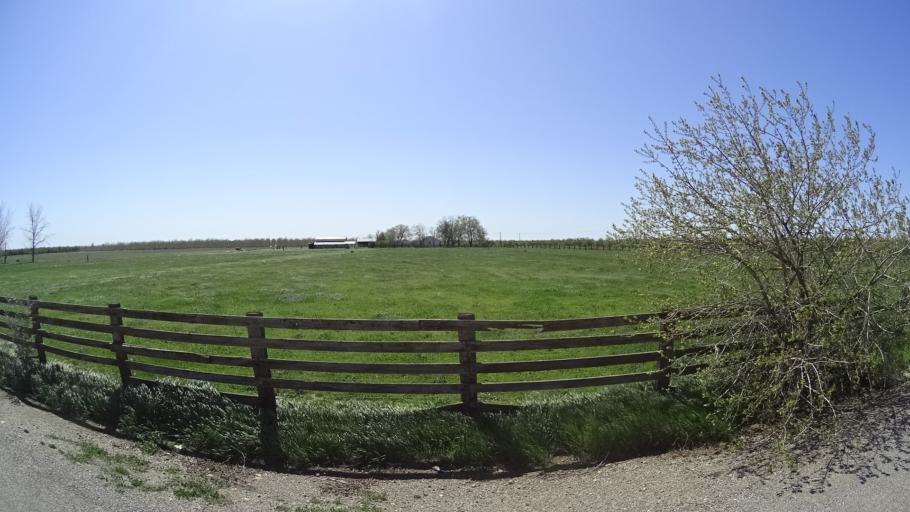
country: US
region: California
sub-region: Glenn County
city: Orland
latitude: 39.7969
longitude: -122.1234
